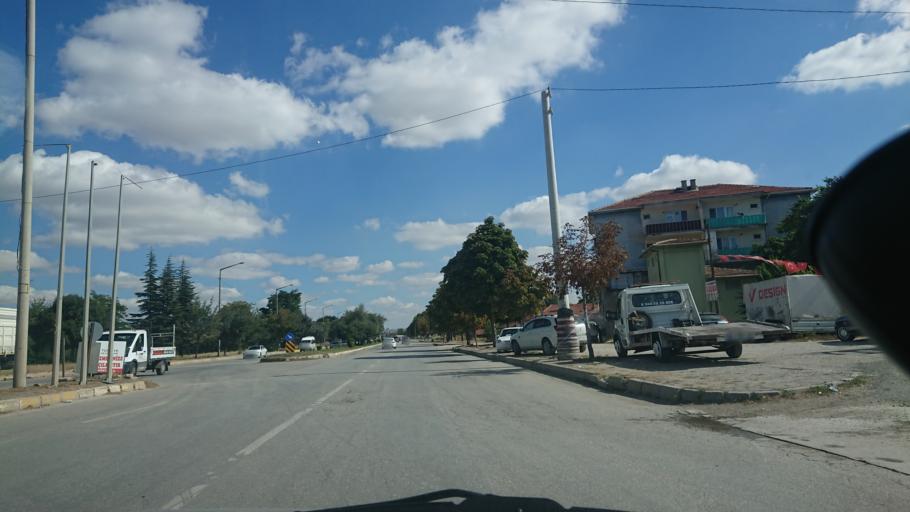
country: TR
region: Eskisehir
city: Eskisehir
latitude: 39.7596
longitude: 30.5697
